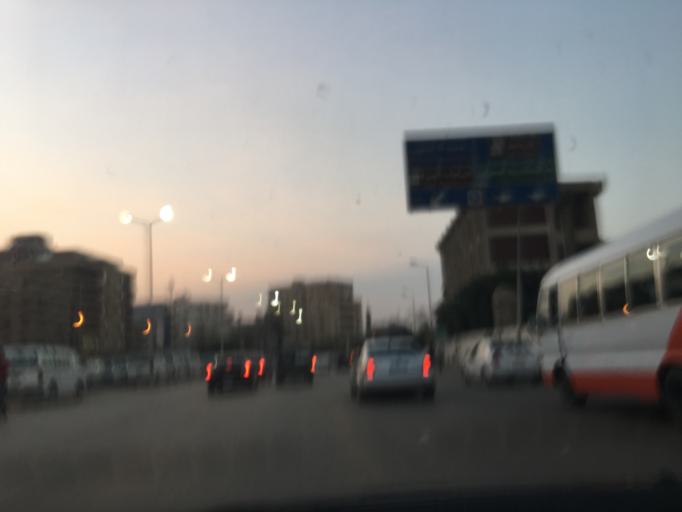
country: EG
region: Al Jizah
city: Al Jizah
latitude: 29.9908
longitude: 31.1321
